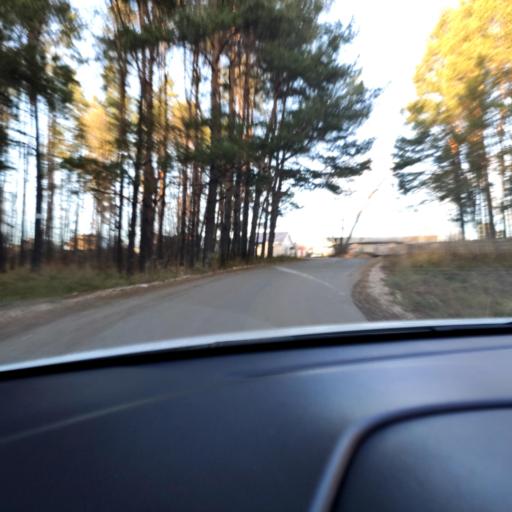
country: RU
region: Tatarstan
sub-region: Gorod Kazan'
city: Kazan
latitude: 55.8875
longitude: 49.0564
